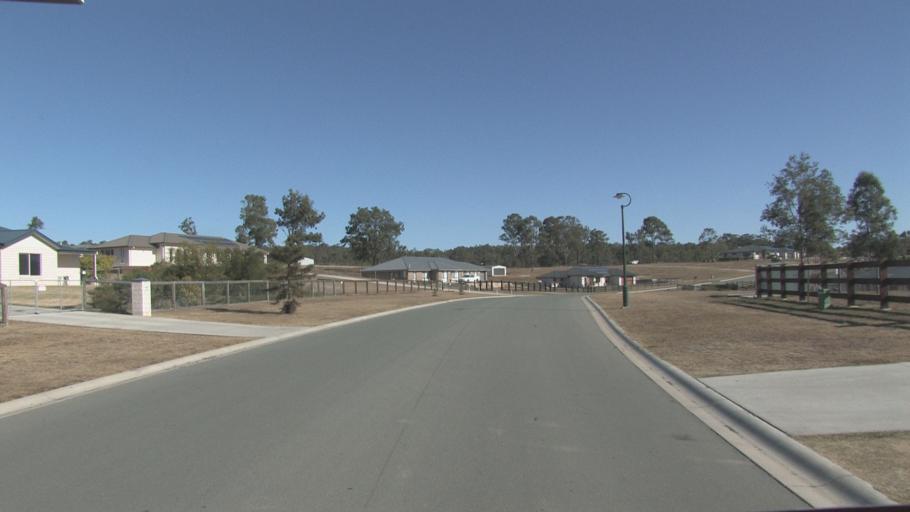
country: AU
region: Queensland
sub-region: Logan
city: Cedar Vale
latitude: -27.8716
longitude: 153.0473
